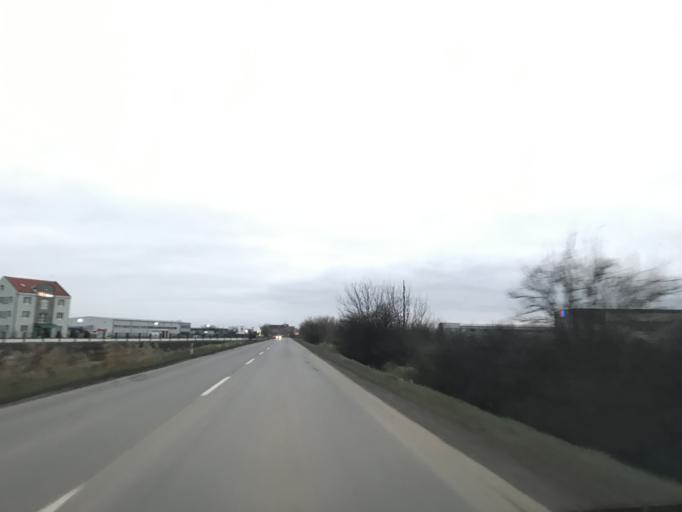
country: RS
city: Rumenka
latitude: 45.2852
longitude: 19.7634
